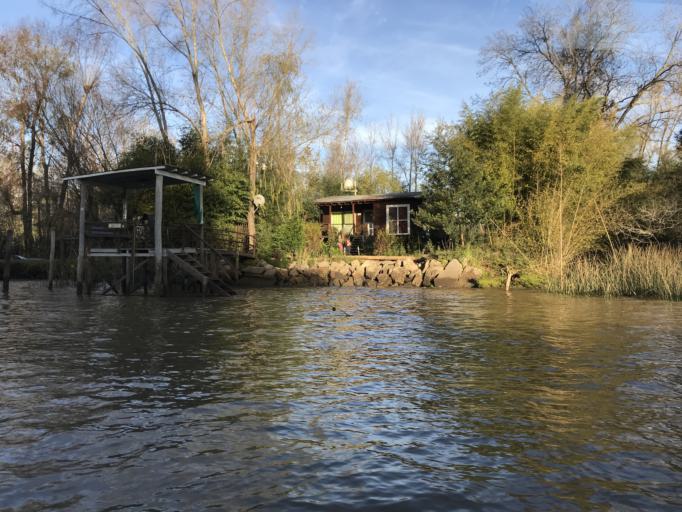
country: AR
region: Buenos Aires
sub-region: Partido de Tigre
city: Tigre
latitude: -34.3738
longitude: -58.5863
